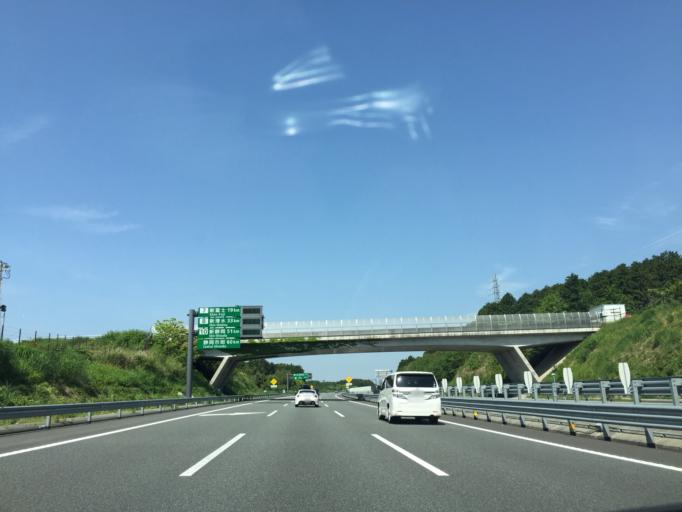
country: JP
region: Shizuoka
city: Numazu
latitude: 35.1520
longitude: 138.8511
